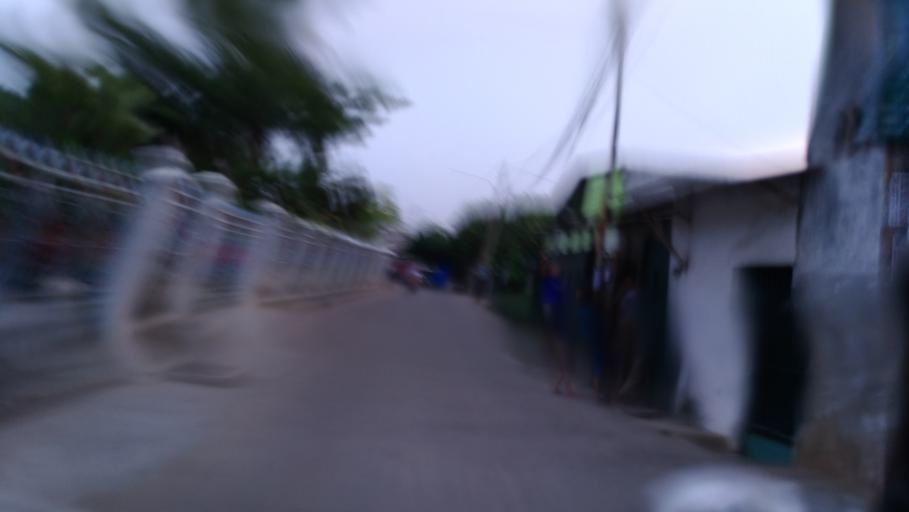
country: ID
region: West Java
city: Depok
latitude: -6.3592
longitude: 106.8669
